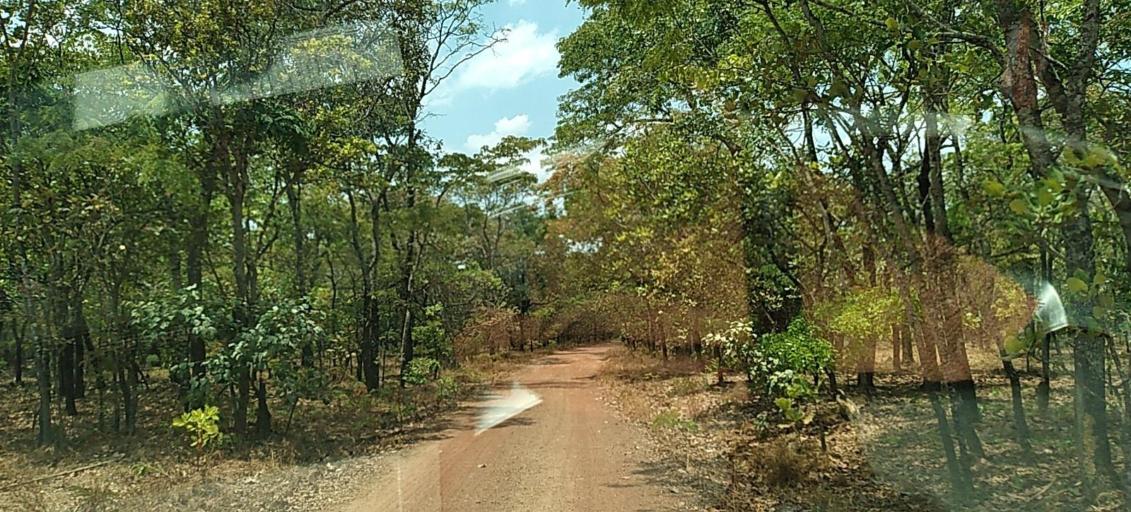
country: ZM
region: Copperbelt
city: Chililabombwe
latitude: -12.5098
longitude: 27.6315
